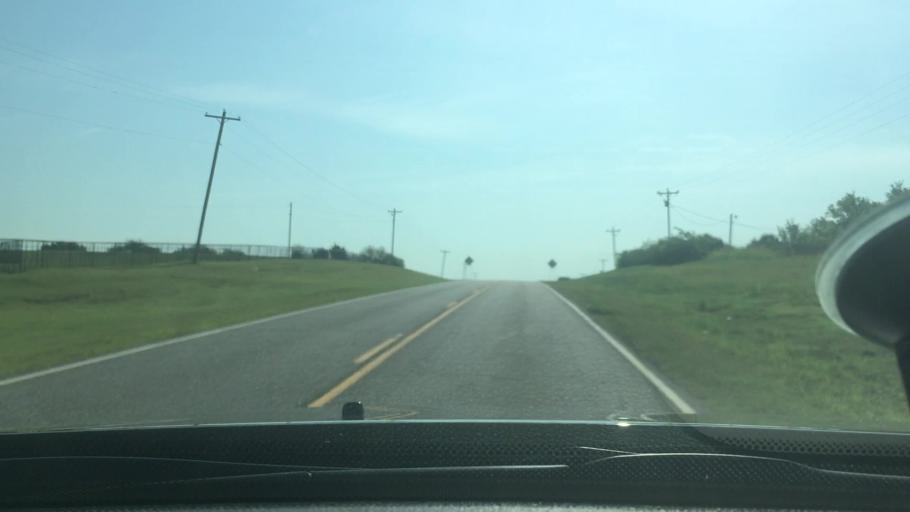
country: US
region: Oklahoma
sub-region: Garvin County
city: Wynnewood
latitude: 34.6518
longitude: -97.2467
